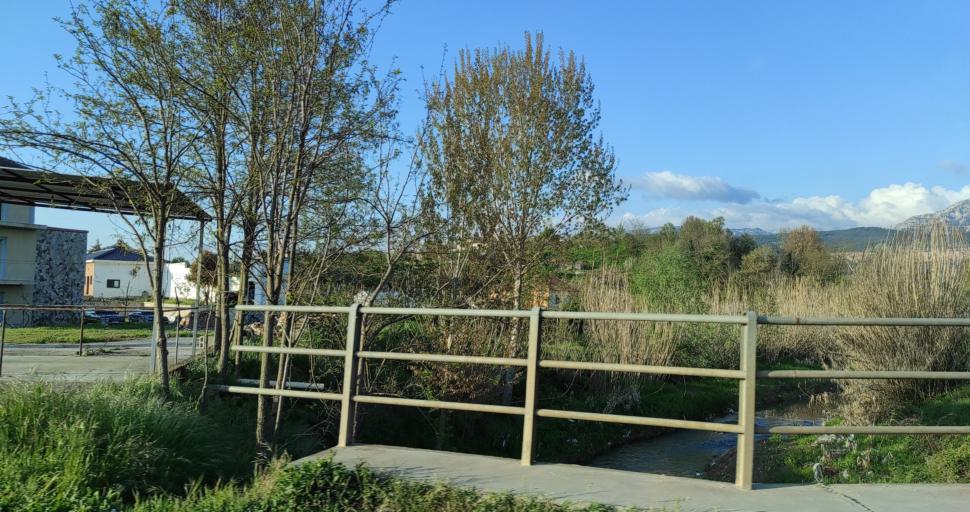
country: AL
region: Durres
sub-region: Rrethi i Krujes
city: Fushe-Kruje
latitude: 41.4907
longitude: 19.7229
